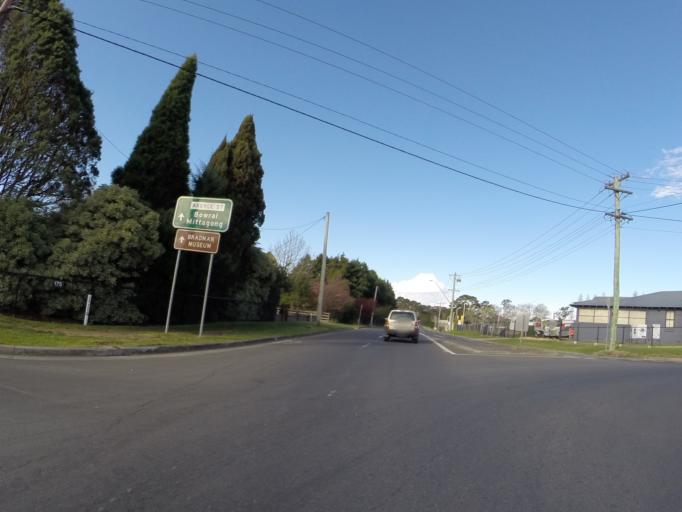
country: AU
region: New South Wales
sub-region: Wingecarribee
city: Moss Vale
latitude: -34.5457
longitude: 150.3791
